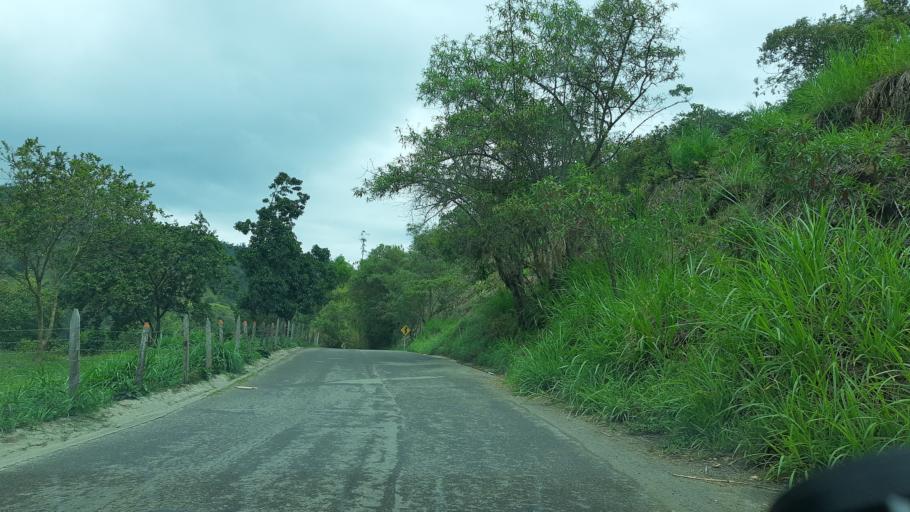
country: CO
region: Cundinamarca
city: Tenza
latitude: 5.0856
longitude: -73.4351
